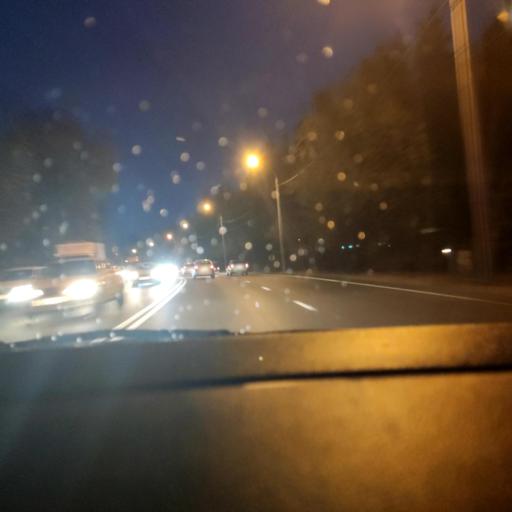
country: RU
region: Voronezj
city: Pridonskoy
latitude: 51.6786
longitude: 39.1149
